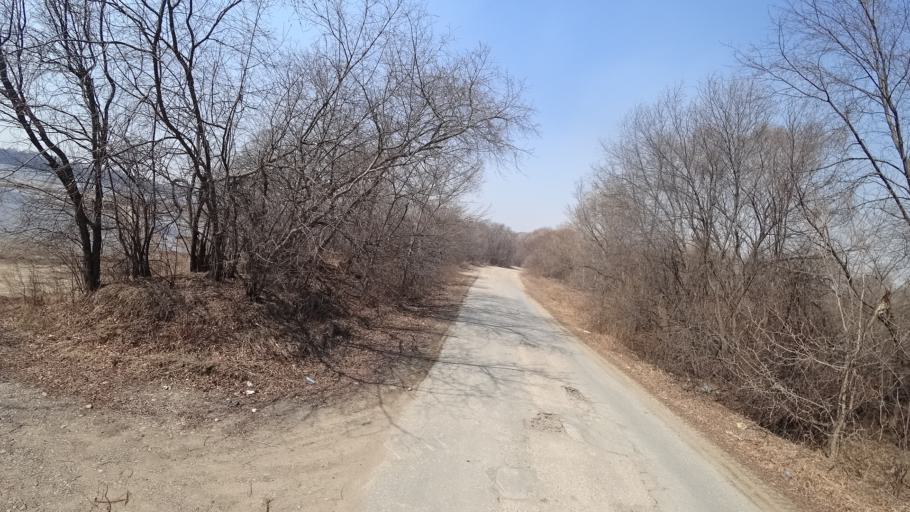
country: RU
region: Amur
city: Novobureyskiy
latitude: 49.7885
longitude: 129.9091
